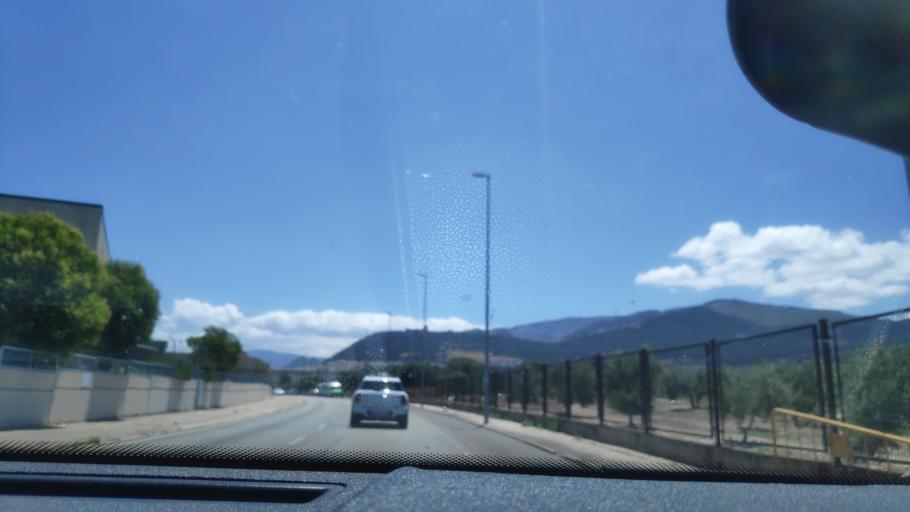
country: ES
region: Andalusia
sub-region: Provincia de Jaen
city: Jaen
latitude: 37.7973
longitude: -3.7929
